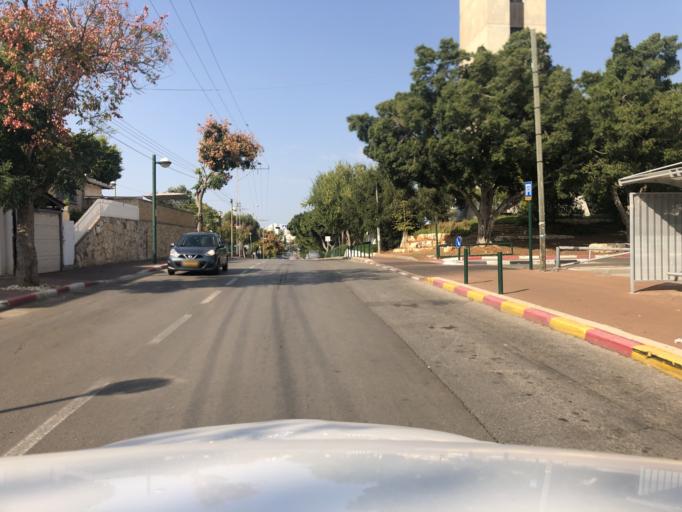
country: IL
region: Central District
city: Kfar Saba
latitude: 32.1838
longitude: 34.9100
